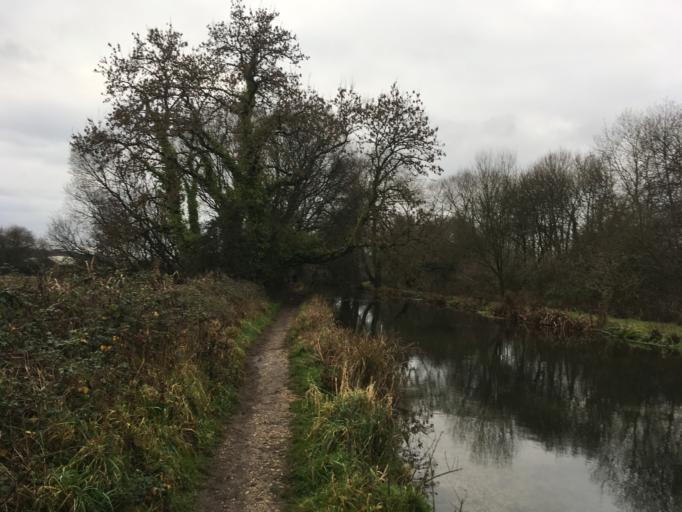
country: GB
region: England
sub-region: Hampshire
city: Eastleigh
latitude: 50.9916
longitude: -1.3416
